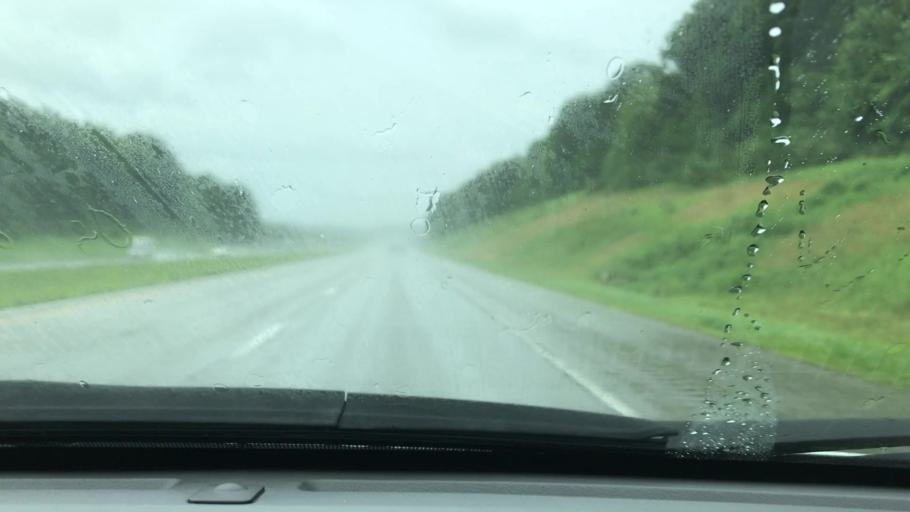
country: US
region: Pennsylvania
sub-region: Blair County
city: Tyrone
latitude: 40.6939
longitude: -78.2191
